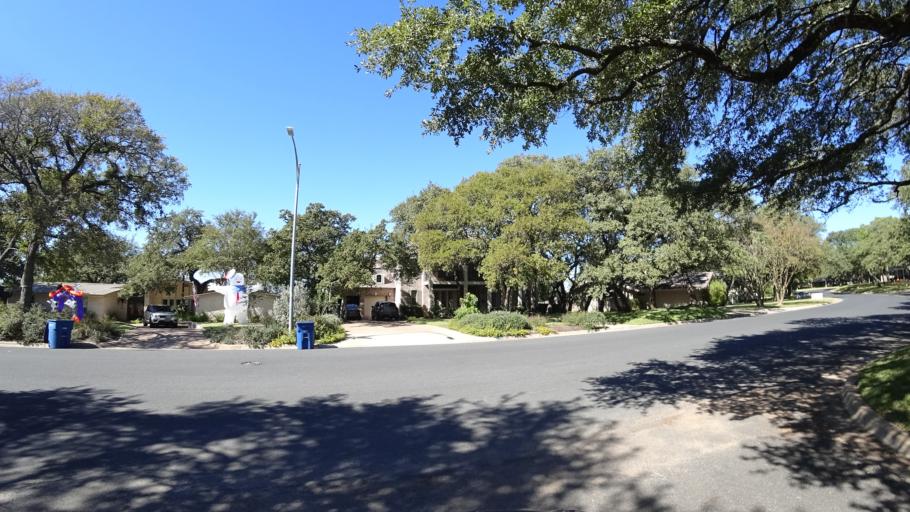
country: US
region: Texas
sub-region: Travis County
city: West Lake Hills
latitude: 30.3621
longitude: -97.7705
